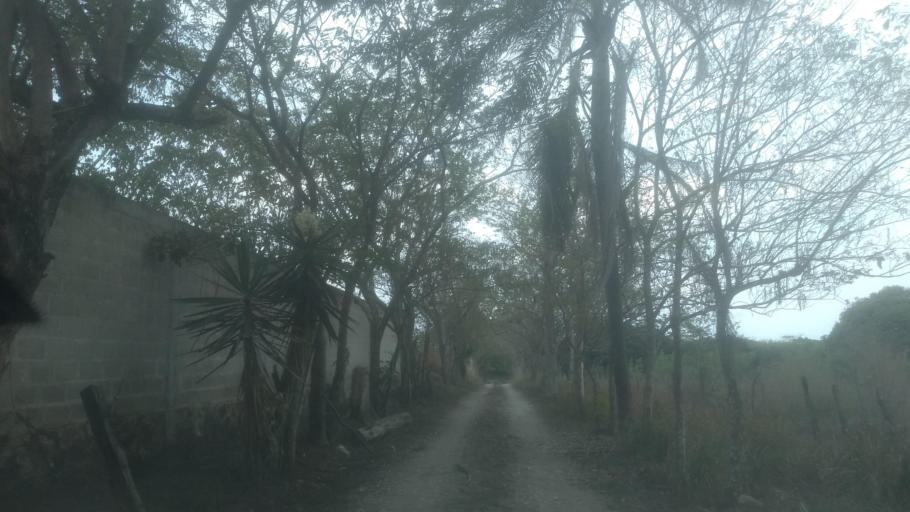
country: MX
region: Veracruz
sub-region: Emiliano Zapata
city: Plan del Rio
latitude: 19.4318
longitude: -96.6972
